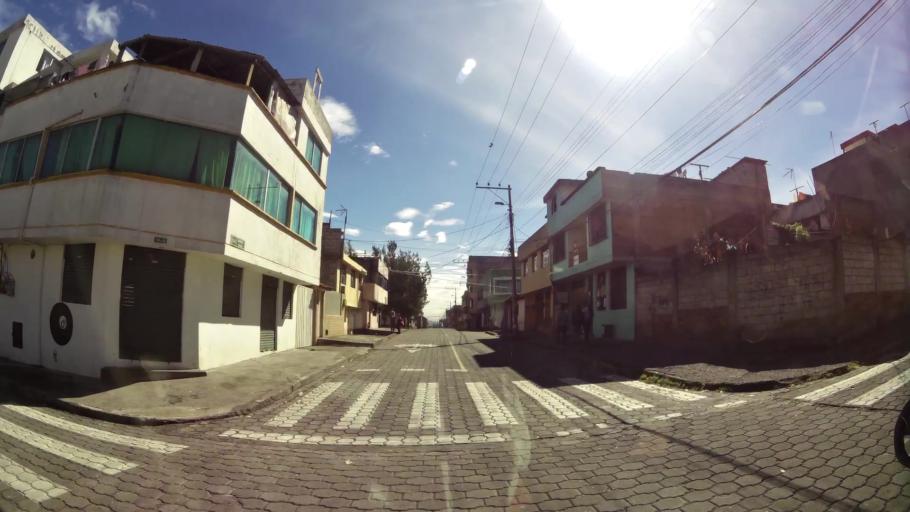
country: EC
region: Pichincha
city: Quito
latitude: -0.3005
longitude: -78.5637
